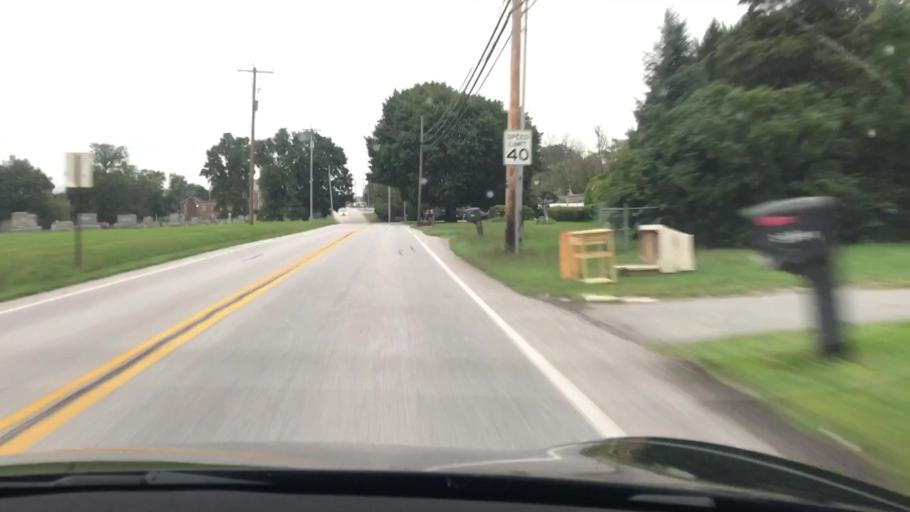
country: US
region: Pennsylvania
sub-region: York County
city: Dover
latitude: 39.9884
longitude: -76.8613
